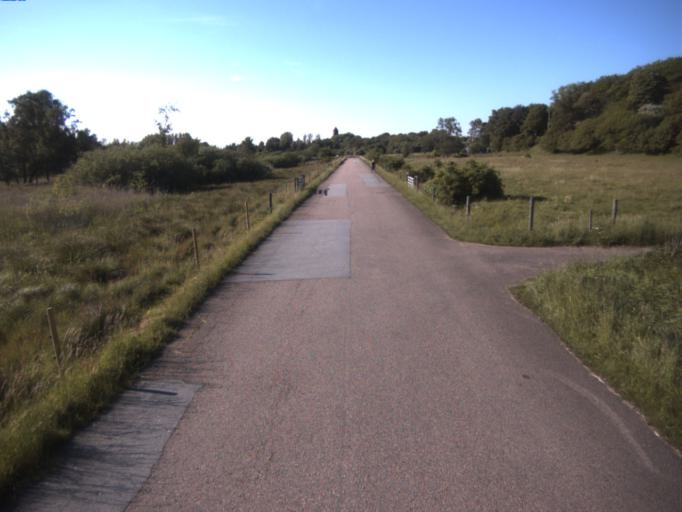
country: SE
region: Skane
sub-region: Helsingborg
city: Rydeback
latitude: 55.9865
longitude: 12.7563
